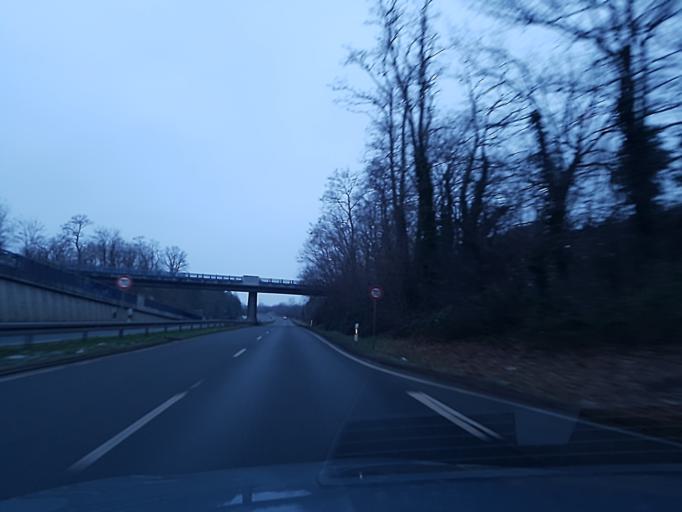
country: DE
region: Saxony
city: Riesa
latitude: 51.3035
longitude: 13.2850
